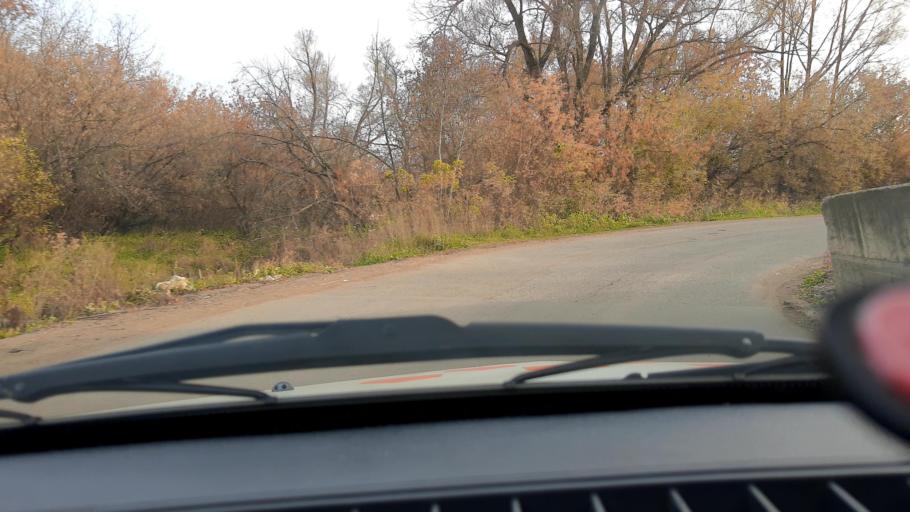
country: RU
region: Bashkortostan
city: Iglino
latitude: 54.7995
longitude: 56.3142
